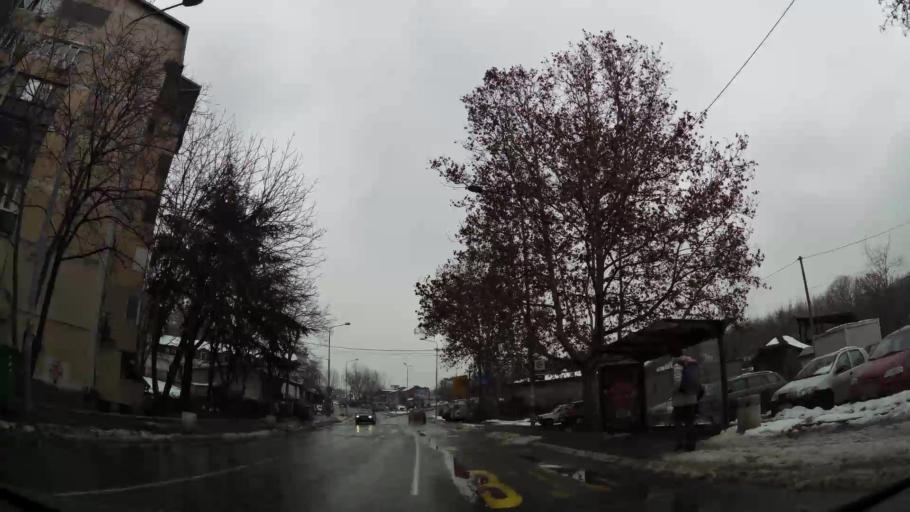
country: RS
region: Central Serbia
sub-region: Belgrade
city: Vozdovac
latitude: 44.7660
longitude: 20.4914
